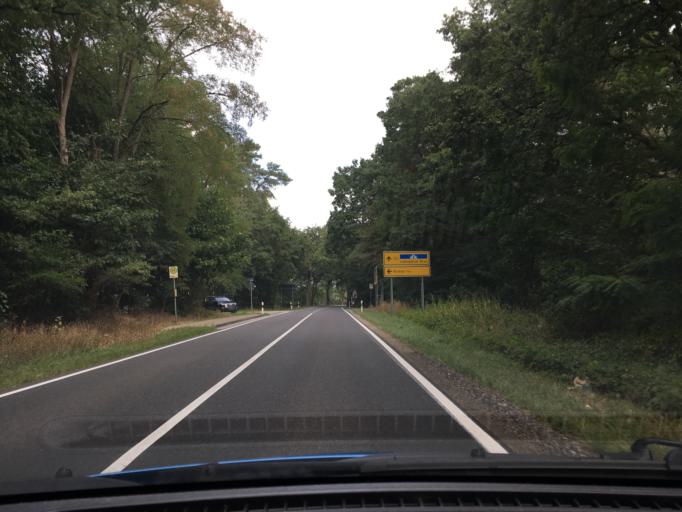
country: DE
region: Mecklenburg-Vorpommern
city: Malliss
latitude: 53.2005
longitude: 11.3024
